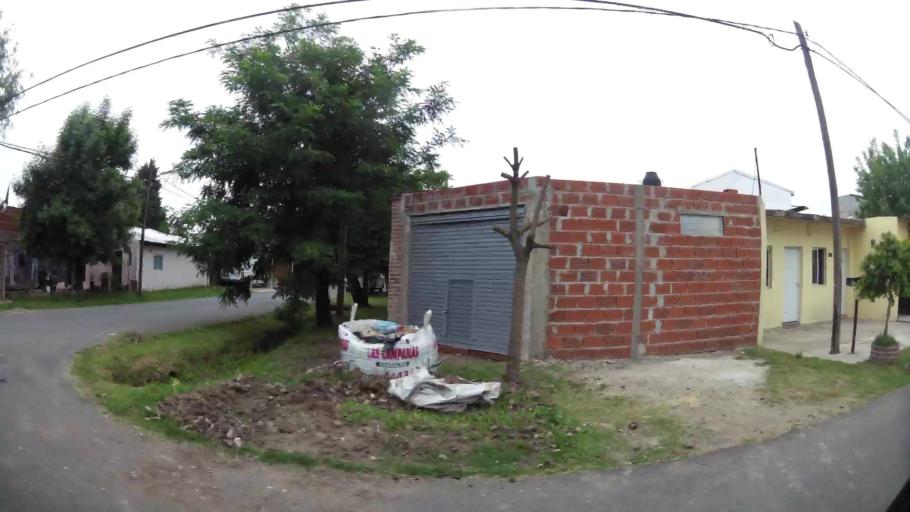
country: AR
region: Buenos Aires
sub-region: Partido de Campana
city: Campana
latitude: -34.1958
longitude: -58.9464
